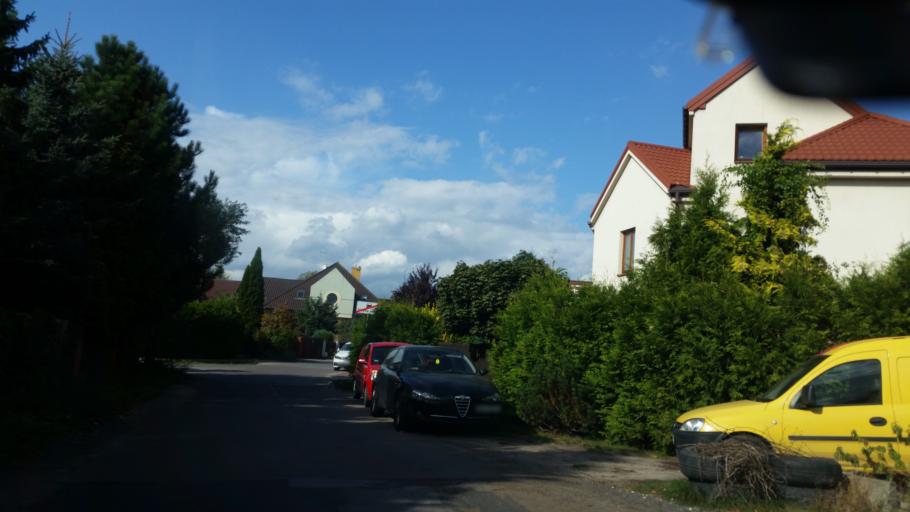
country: PL
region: Masovian Voivodeship
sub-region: Warszawa
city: Targowek
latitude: 52.3165
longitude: 21.0433
